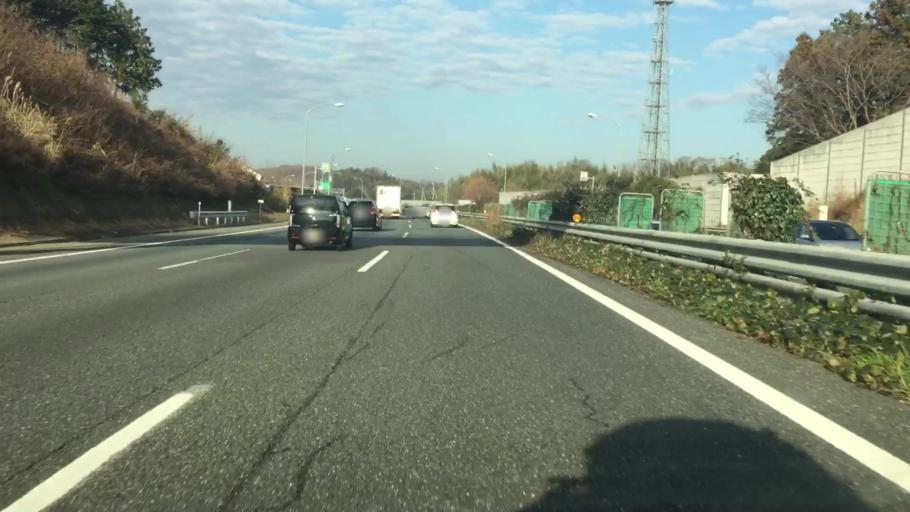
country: JP
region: Saitama
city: Ogawa
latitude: 36.0648
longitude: 139.3229
